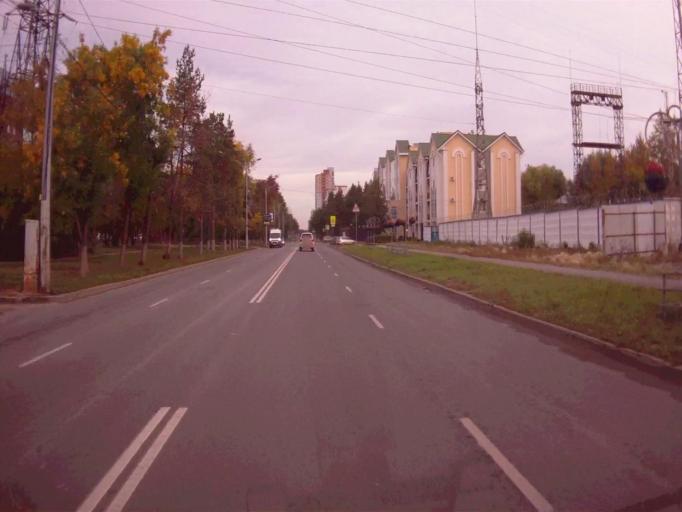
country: RU
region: Chelyabinsk
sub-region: Gorod Chelyabinsk
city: Chelyabinsk
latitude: 55.1497
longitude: 61.3653
